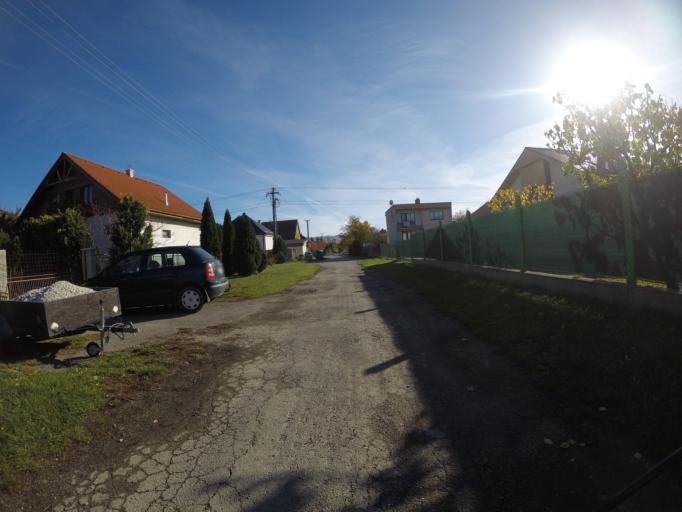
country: SK
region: Trenciansky
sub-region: Okres Nove Mesto nad Vahom
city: Nove Mesto nad Vahom
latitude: 48.7471
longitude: 17.8272
